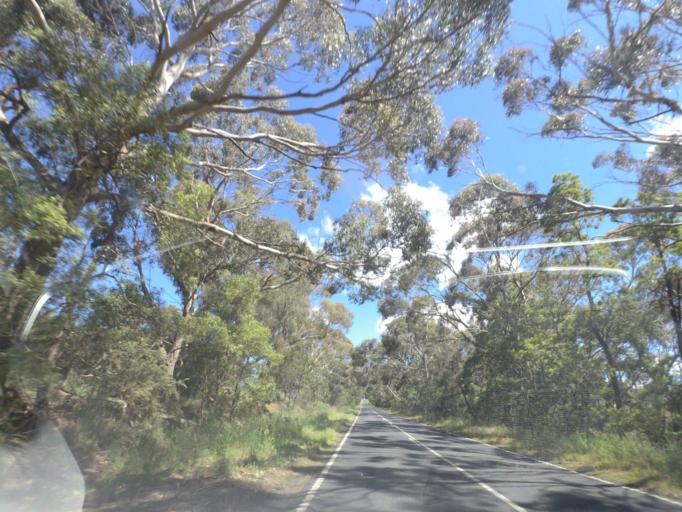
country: AU
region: Victoria
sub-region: Mount Alexander
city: Castlemaine
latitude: -37.3145
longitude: 144.4086
